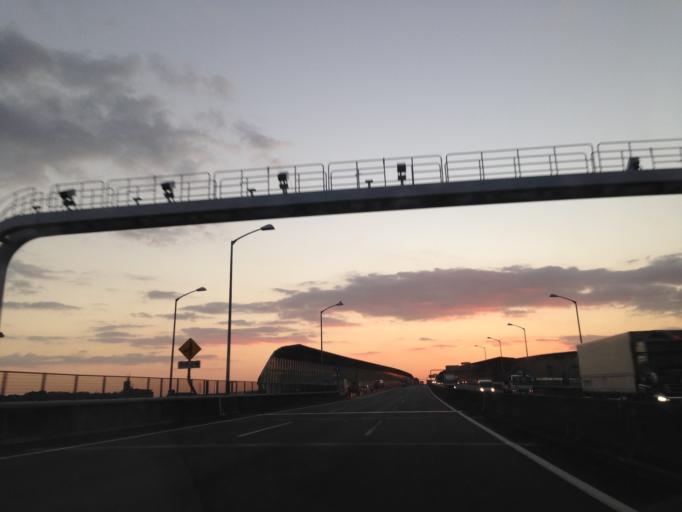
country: JP
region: Aichi
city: Obu
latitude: 35.0506
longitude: 136.9058
